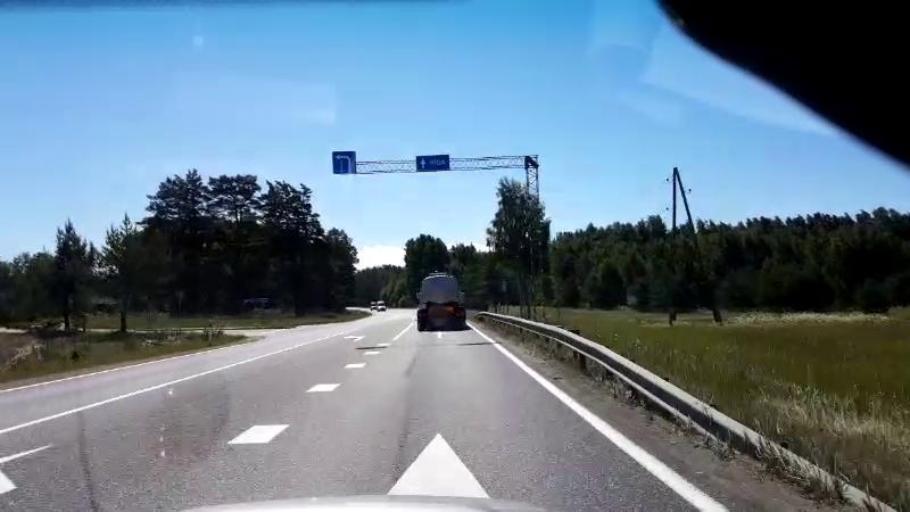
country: LV
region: Saulkrastu
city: Saulkrasti
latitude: 57.3846
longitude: 24.4297
